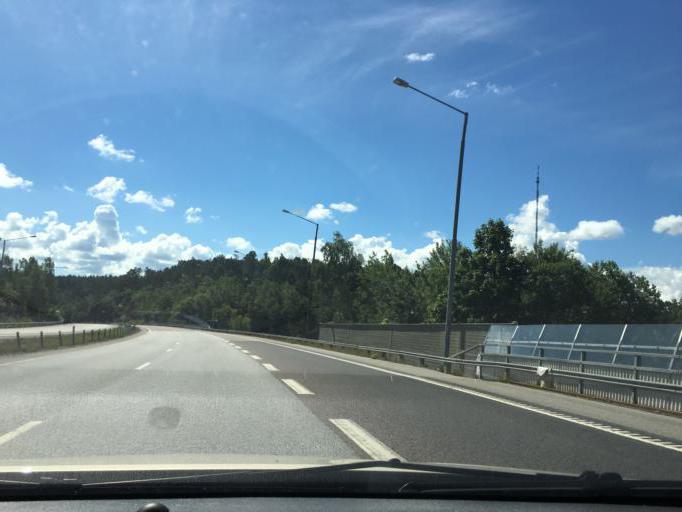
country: SE
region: Stockholm
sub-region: Nacka Kommun
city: Nacka
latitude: 59.3059
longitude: 18.1814
